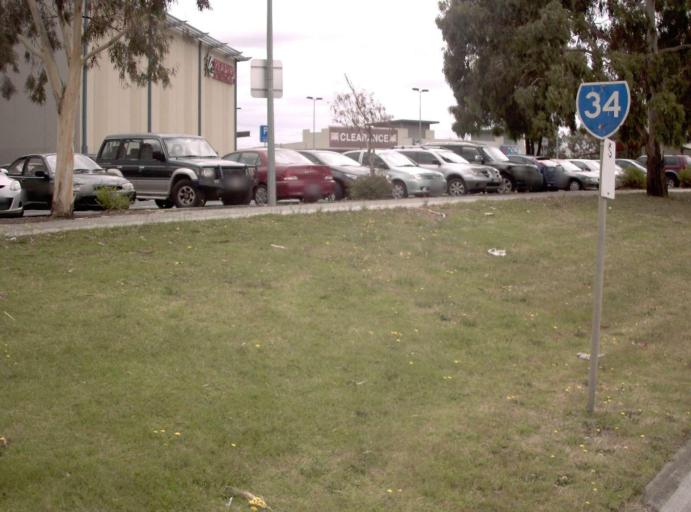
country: AU
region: Victoria
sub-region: Yarra Ranges
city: Chirnside Park
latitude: -37.7609
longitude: 145.3107
